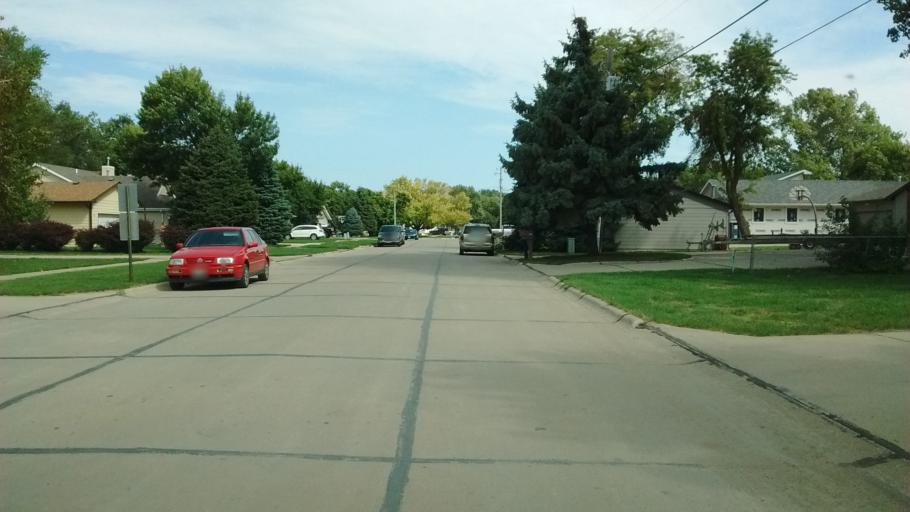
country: US
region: South Dakota
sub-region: Union County
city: North Sioux City
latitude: 42.5435
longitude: -96.5248
